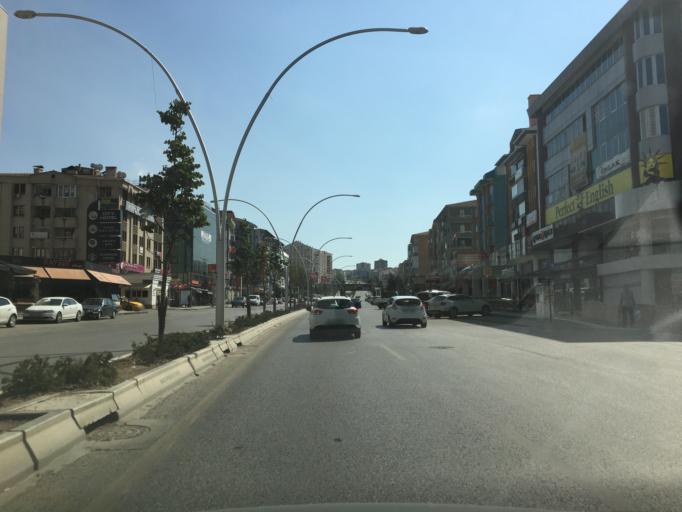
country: TR
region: Ankara
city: Cankaya
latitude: 39.8755
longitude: 32.8633
